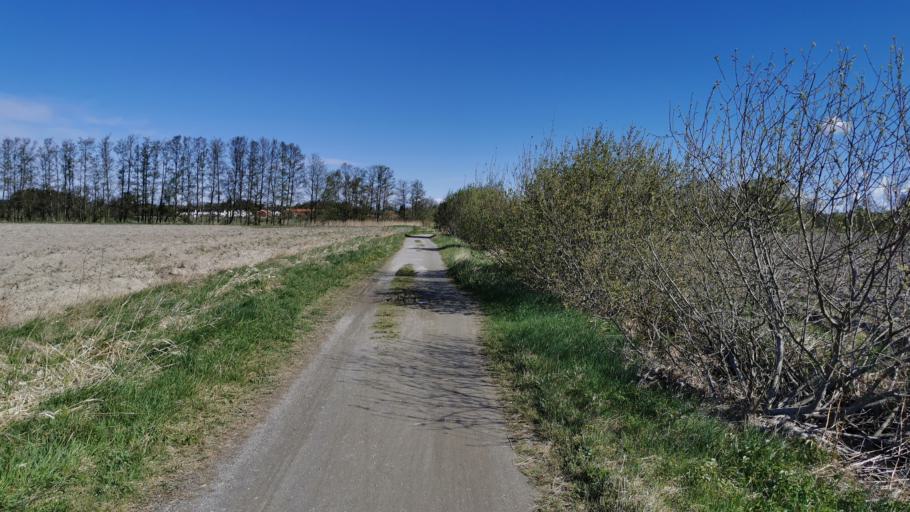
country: SE
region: OErebro
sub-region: Orebro Kommun
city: Orebro
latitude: 59.3069
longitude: 15.2165
